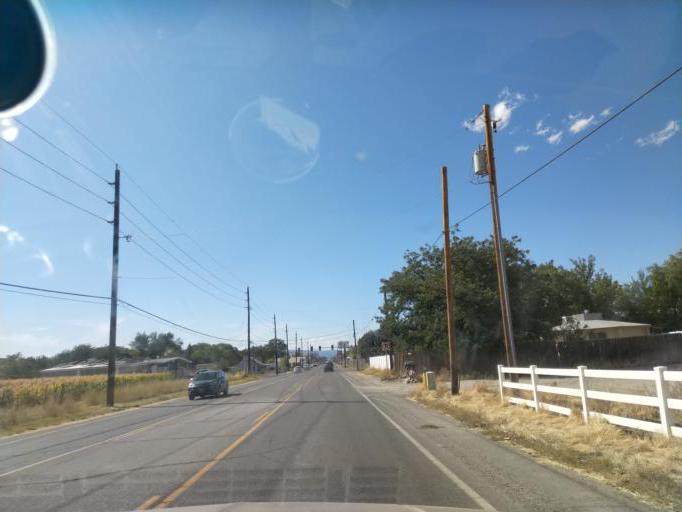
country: US
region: Colorado
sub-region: Mesa County
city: Clifton
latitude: 39.0918
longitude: -108.4436
